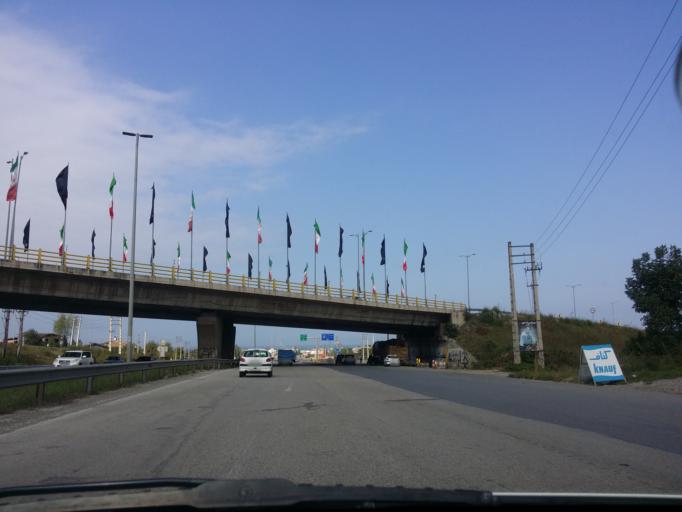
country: IR
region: Mazandaran
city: Chalus
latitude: 36.6518
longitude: 51.4055
